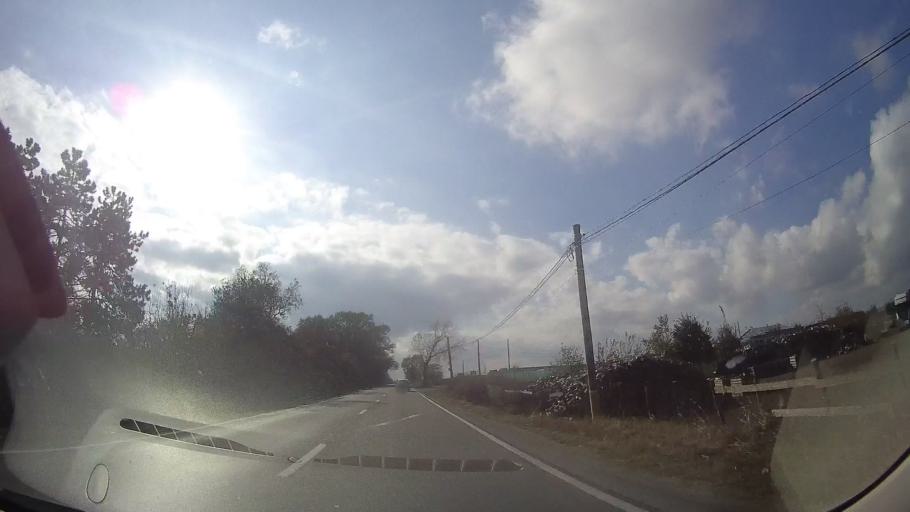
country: RO
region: Constanta
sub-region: Comuna Agigea
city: Agigea
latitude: 44.0852
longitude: 28.6074
